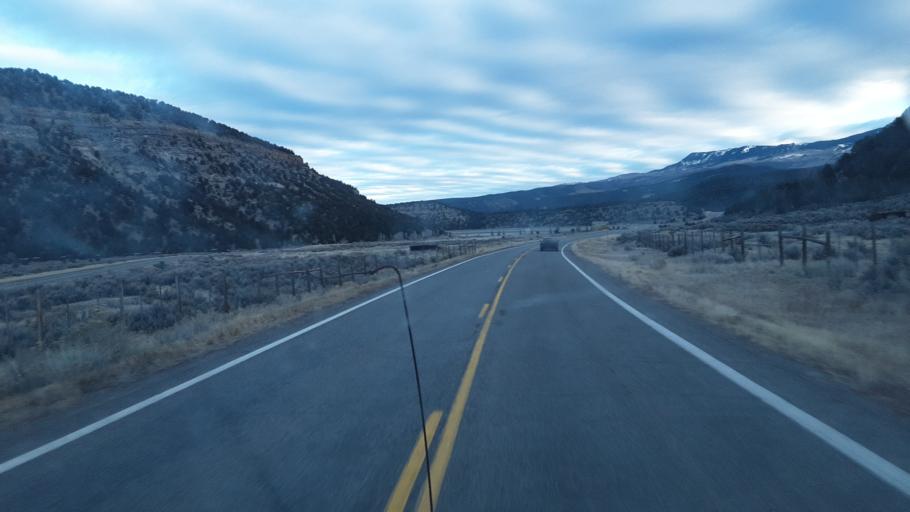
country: US
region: Colorado
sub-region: Ouray County
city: Ouray
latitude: 38.1926
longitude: -107.7444
